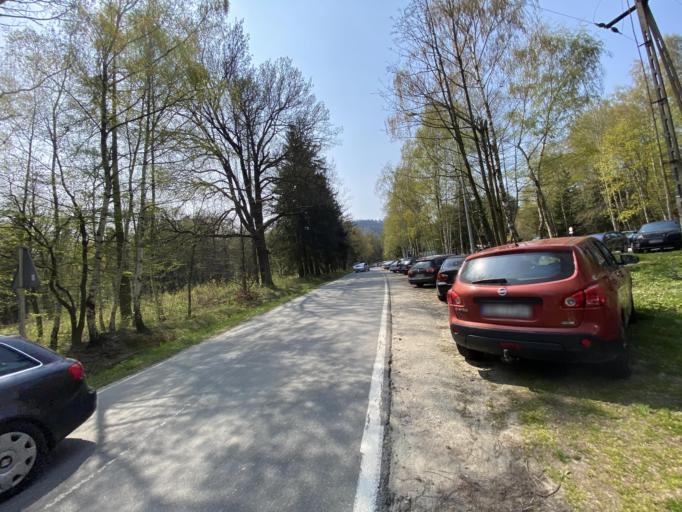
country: PL
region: Lower Silesian Voivodeship
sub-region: Powiat wroclawski
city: Sobotka
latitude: 50.8462
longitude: 16.7285
